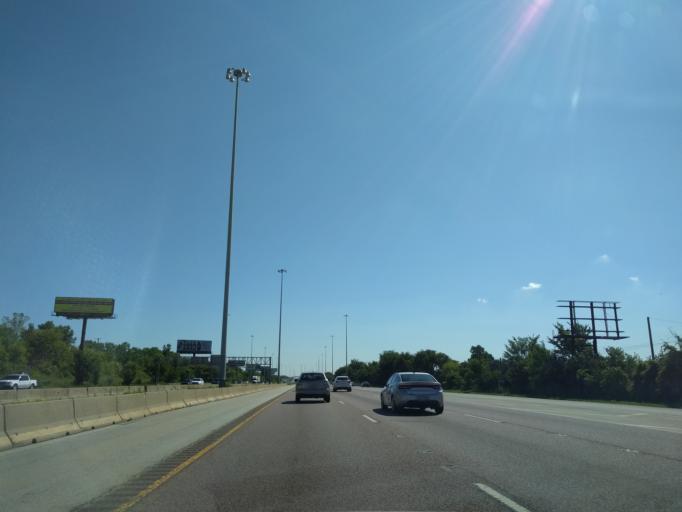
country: US
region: Illinois
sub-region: Cook County
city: Stickney
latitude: 41.8119
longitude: -87.7594
